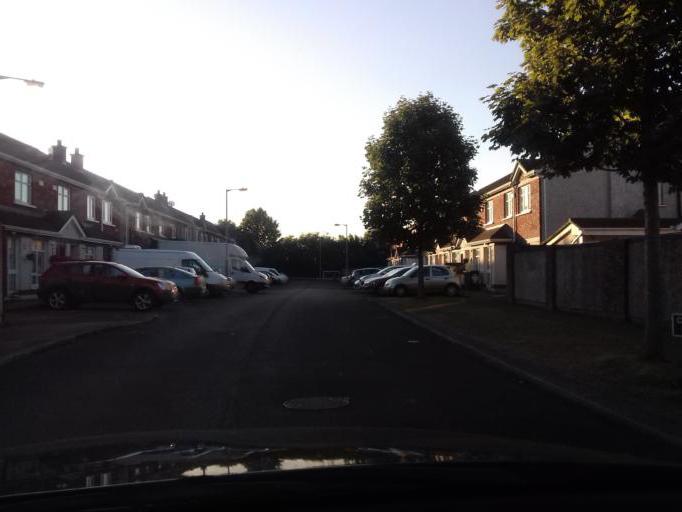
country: IE
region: Leinster
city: Hartstown
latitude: 53.4005
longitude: -6.4393
